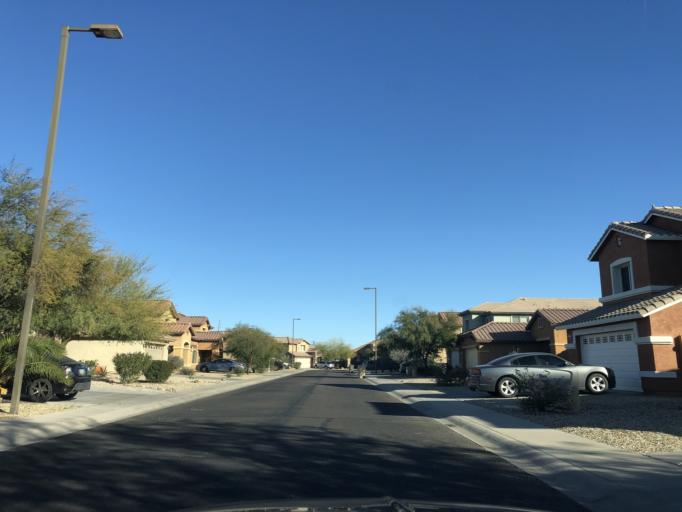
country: US
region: Arizona
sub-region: Maricopa County
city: Buckeye
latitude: 33.4273
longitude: -112.6057
